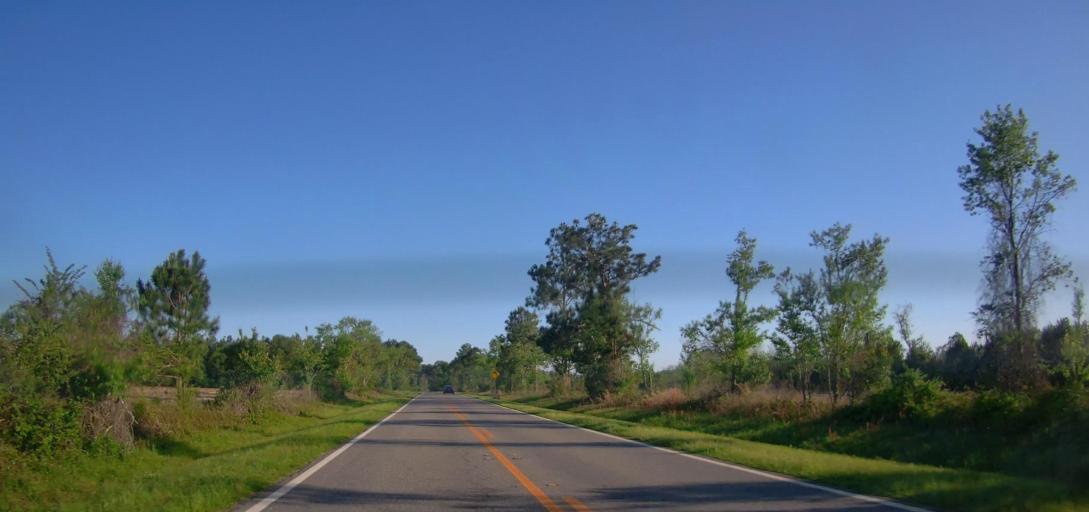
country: US
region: Georgia
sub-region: Ben Hill County
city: Fitzgerald
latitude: 31.6746
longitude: -83.1922
